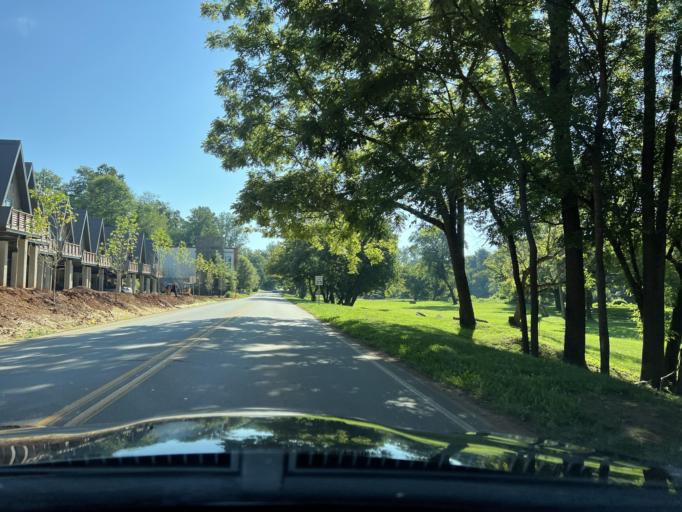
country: US
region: North Carolina
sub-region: Buncombe County
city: Asheville
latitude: 35.5672
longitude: -82.5710
